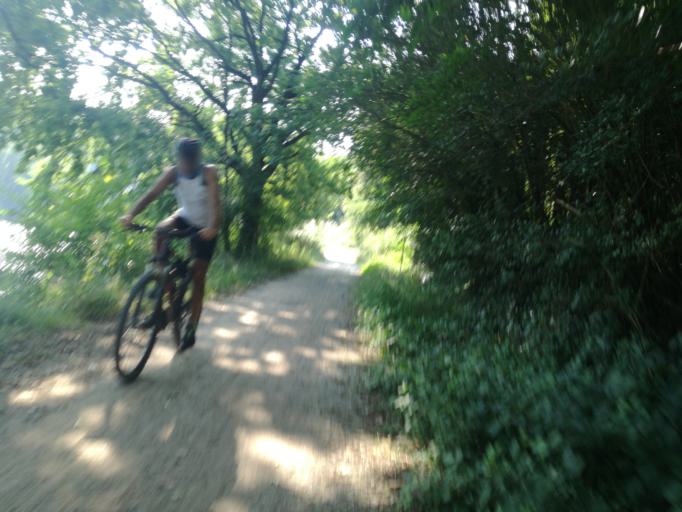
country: IT
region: Lombardy
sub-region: Provincia di Bergamo
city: Suisio
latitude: 45.6493
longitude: 9.4900
